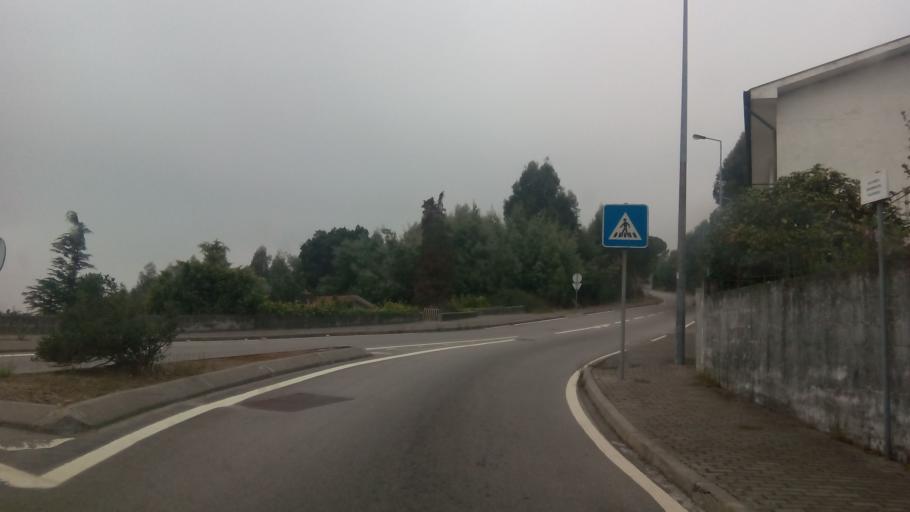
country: PT
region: Porto
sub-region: Paredes
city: Rebordosa
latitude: 41.1939
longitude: -8.4030
